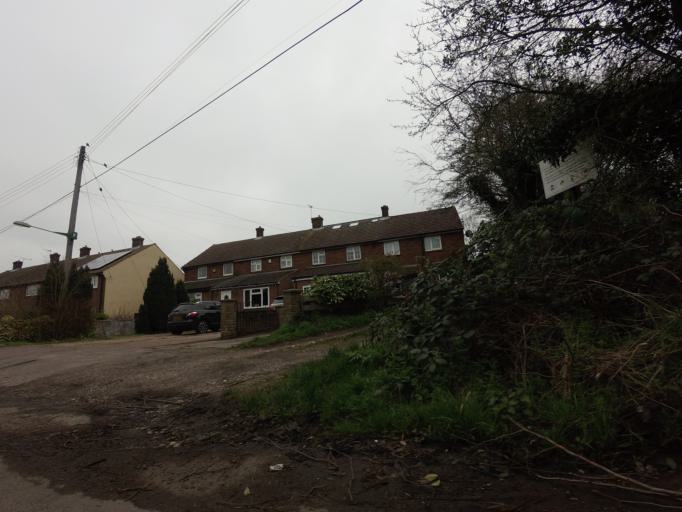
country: GB
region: England
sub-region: Kent
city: Swanley
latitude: 51.3782
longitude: 0.1605
